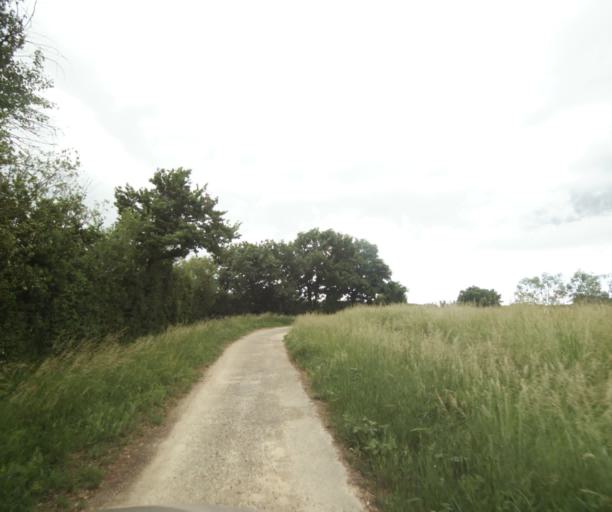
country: FR
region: Rhone-Alpes
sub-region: Departement de l'Ain
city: Tramoyes
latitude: 45.8564
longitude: 4.9545
